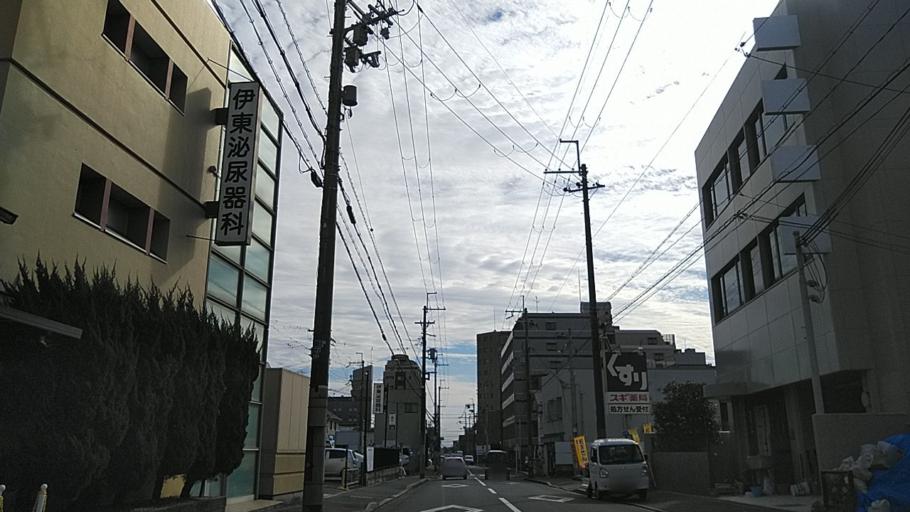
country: JP
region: Kyoto
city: Kyoto
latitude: 35.0053
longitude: 135.7254
